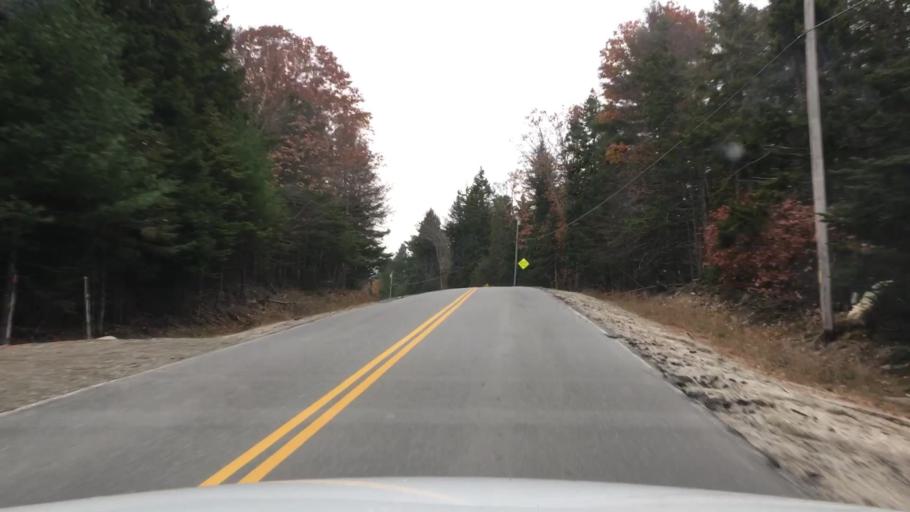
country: US
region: Maine
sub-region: Hancock County
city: Penobscot
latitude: 44.4297
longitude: -68.6262
